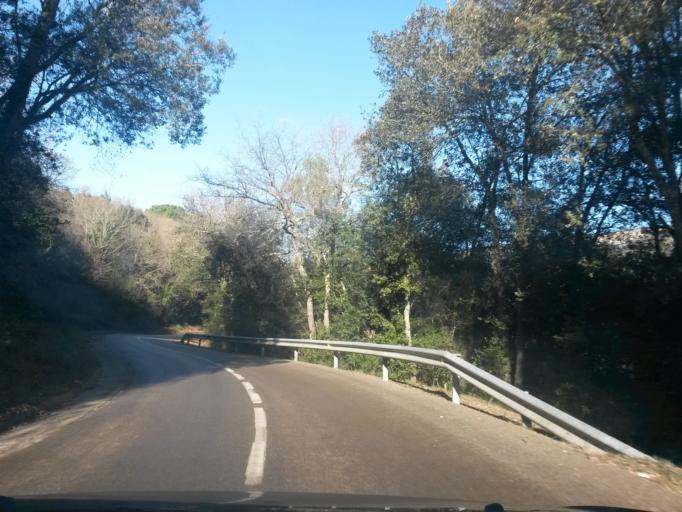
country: ES
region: Catalonia
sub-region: Provincia de Girona
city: la Cellera de Ter
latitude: 42.0207
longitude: 2.6696
